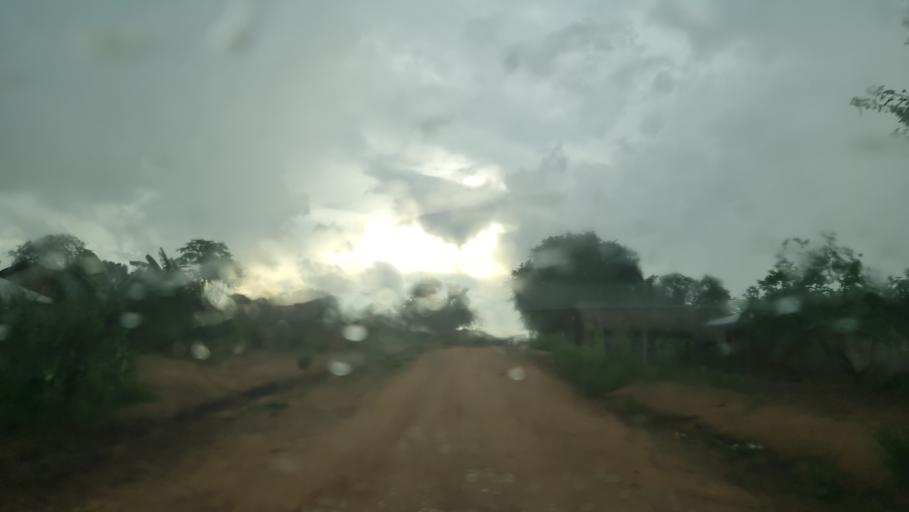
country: MZ
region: Nampula
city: Nacala
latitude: -14.0042
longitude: 40.3511
